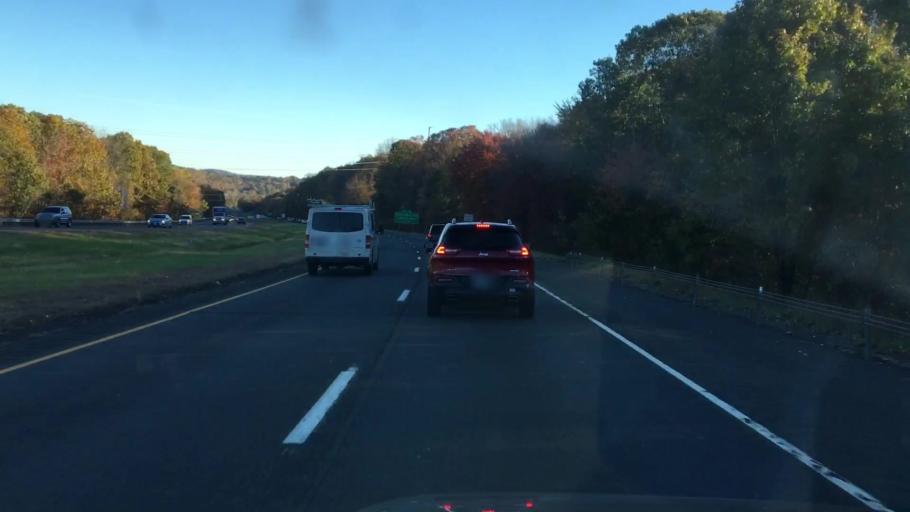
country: US
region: Connecticut
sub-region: Litchfield County
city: Oakville
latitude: 41.5978
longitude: -73.0661
